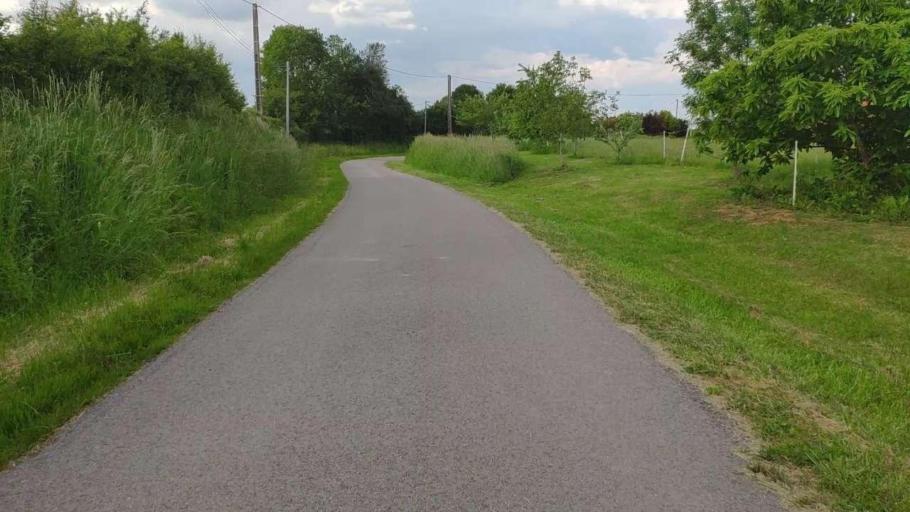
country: FR
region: Franche-Comte
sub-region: Departement du Jura
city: Bletterans
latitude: 46.7958
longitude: 5.3648
